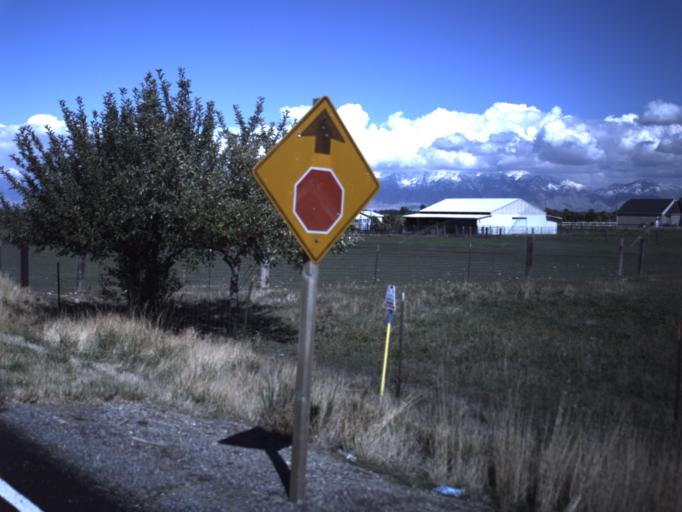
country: US
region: Utah
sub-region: Utah County
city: West Mountain
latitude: 40.0393
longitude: -111.7872
